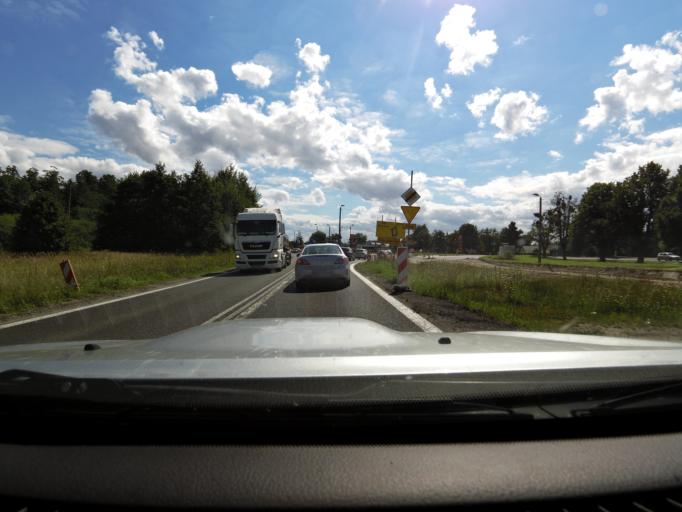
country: PL
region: Warmian-Masurian Voivodeship
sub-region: Powiat ostrodzki
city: Ostroda
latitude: 53.7184
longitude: 19.9491
